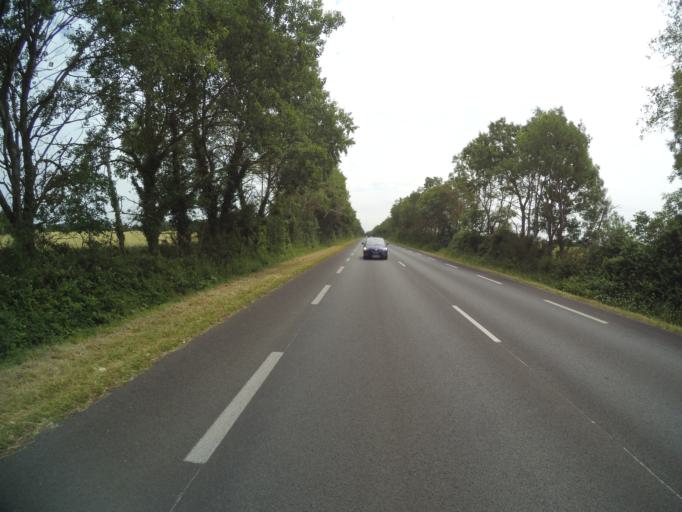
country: FR
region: Pays de la Loire
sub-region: Departement de la Vendee
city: Bouffere
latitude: 46.9361
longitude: -1.3270
